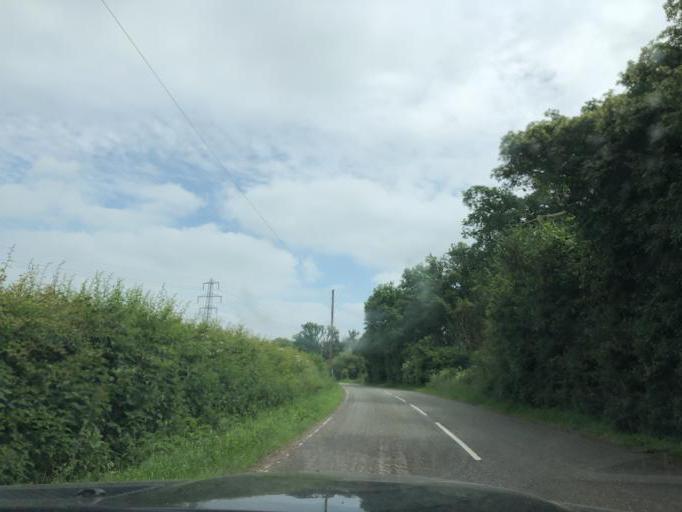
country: GB
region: England
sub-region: Warwickshire
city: Kenilworth
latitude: 52.3314
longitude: -1.6156
